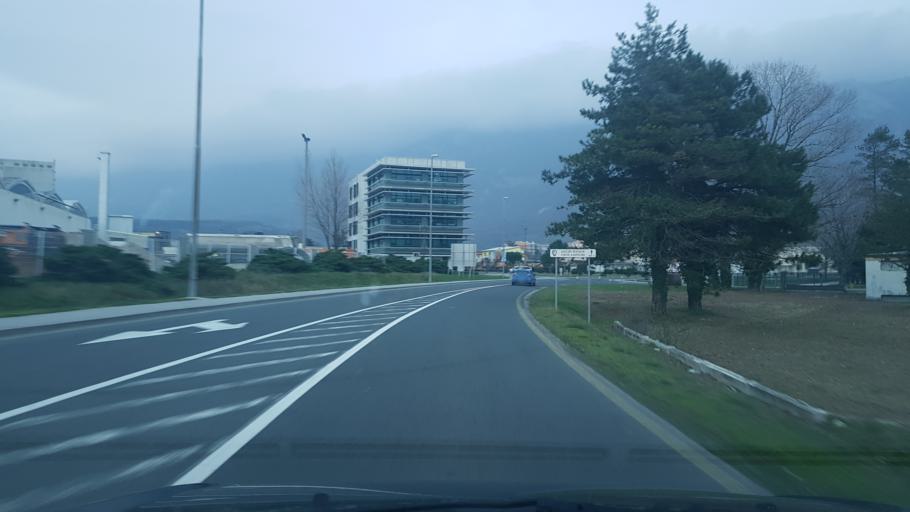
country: SI
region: Ajdovscina
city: Ajdovscina
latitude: 45.8821
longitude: 13.9023
